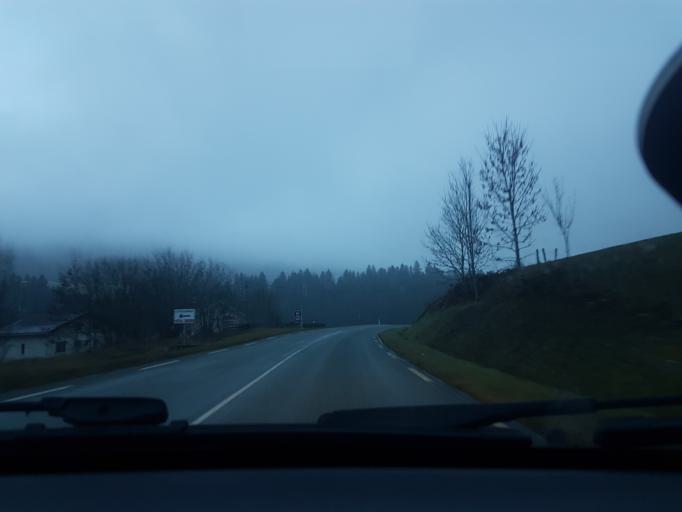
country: FR
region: Franche-Comte
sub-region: Departement du Doubs
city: La Cluse-et-Mijoux
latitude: 46.8947
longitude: 6.4451
